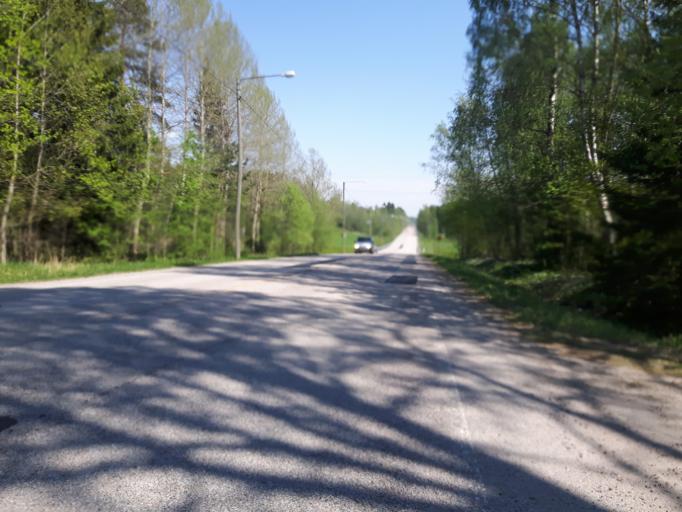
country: FI
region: Uusimaa
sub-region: Helsinki
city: Nickby
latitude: 60.3015
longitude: 25.3651
